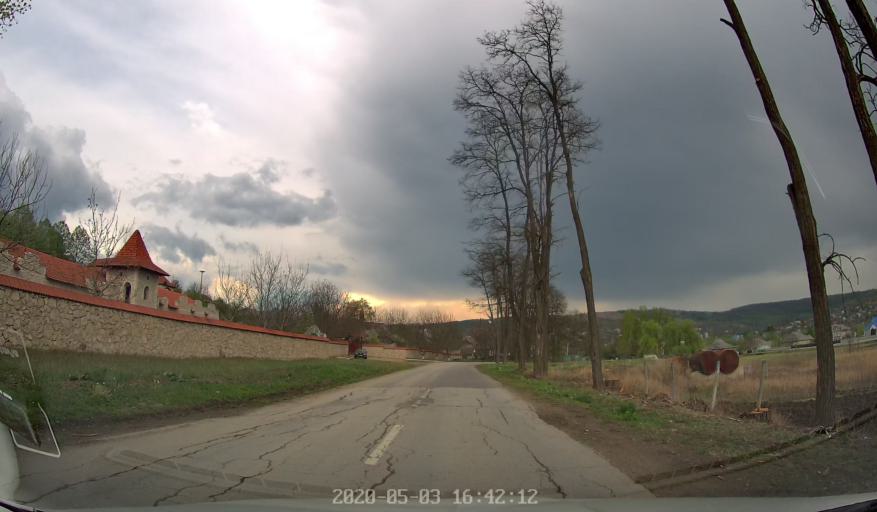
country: MD
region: Stinga Nistrului
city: Bucovat
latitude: 47.1612
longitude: 28.4181
